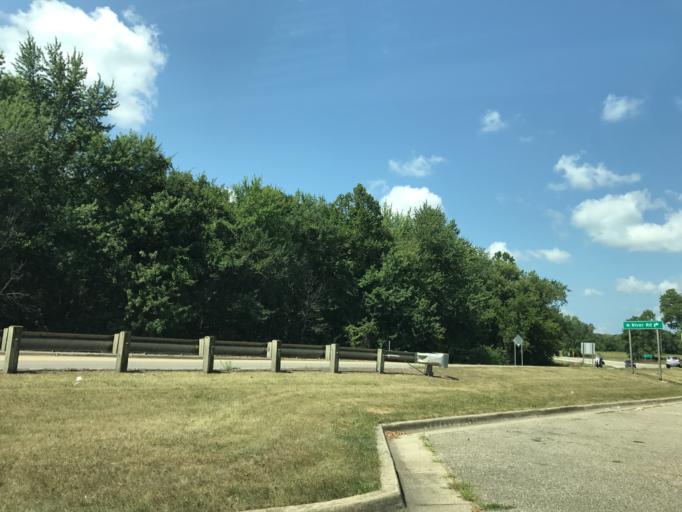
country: US
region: Michigan
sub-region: Saint Joseph County
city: Constantine
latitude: 41.8006
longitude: -85.7576
